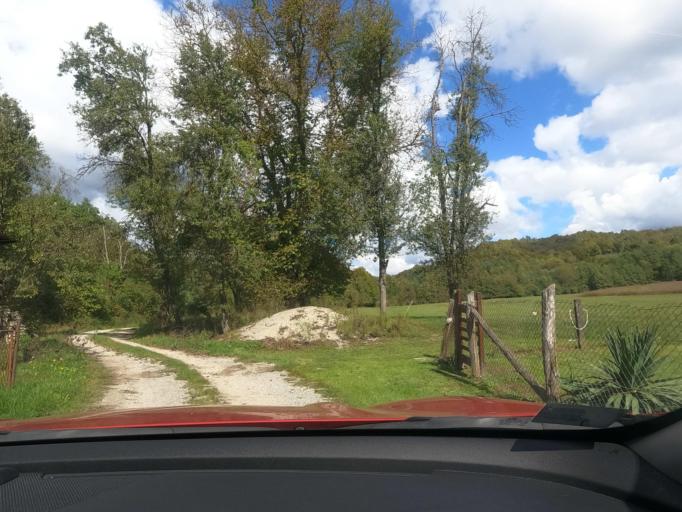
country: BA
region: Federation of Bosnia and Herzegovina
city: Velika Kladusa
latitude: 45.2317
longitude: 15.7738
